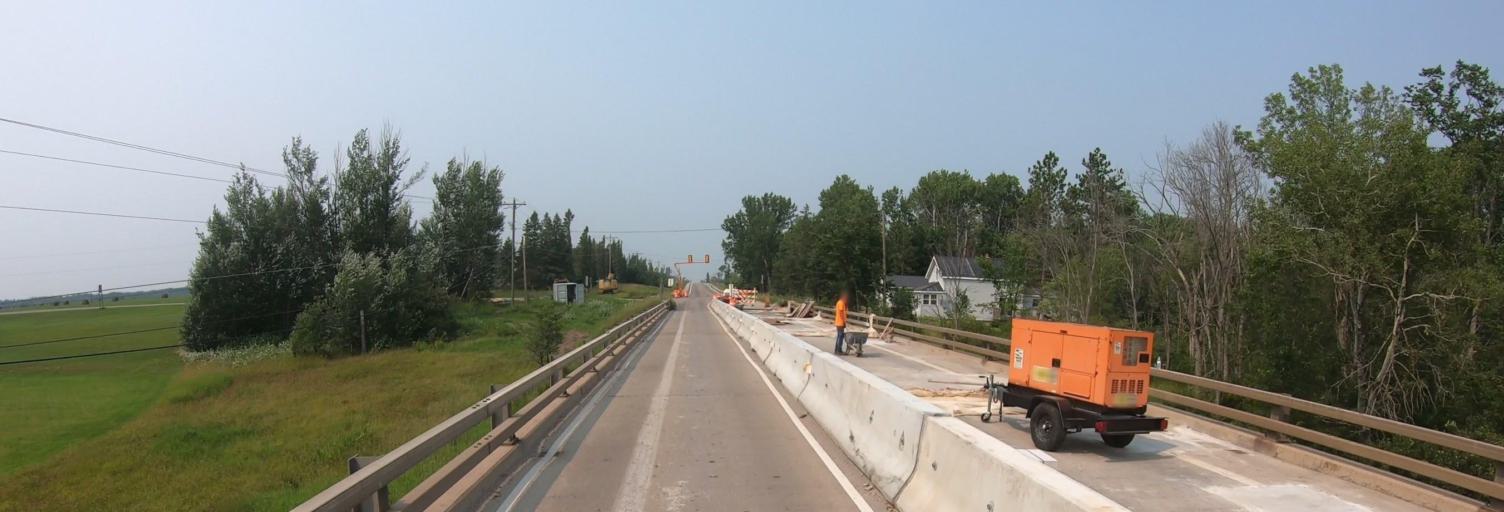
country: US
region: Michigan
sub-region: Chippewa County
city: Sault Ste. Marie
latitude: 46.1432
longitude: -84.3634
